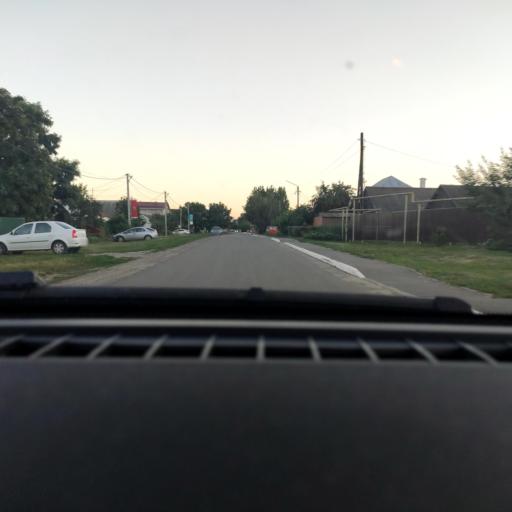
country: RU
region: Voronezj
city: Novaya Usman'
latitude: 51.6595
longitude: 39.3402
